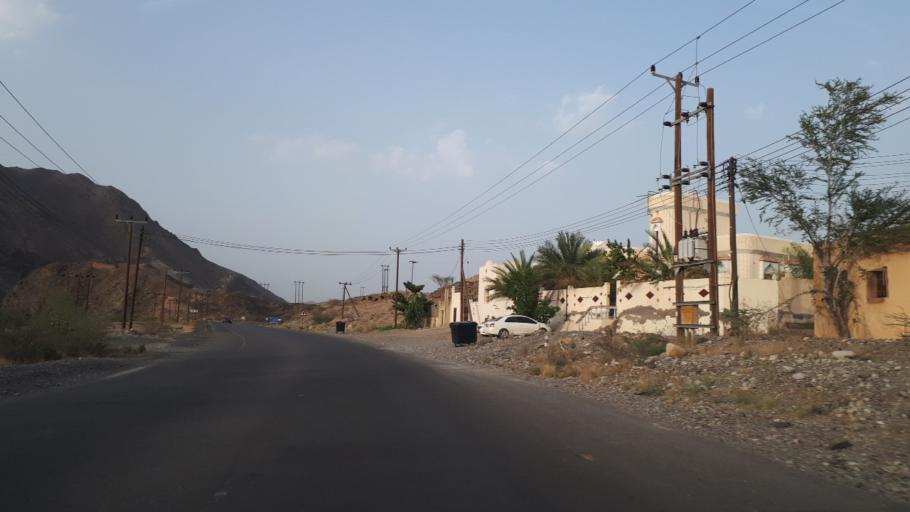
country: OM
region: Al Batinah
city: Rustaq
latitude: 23.3885
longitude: 57.2160
